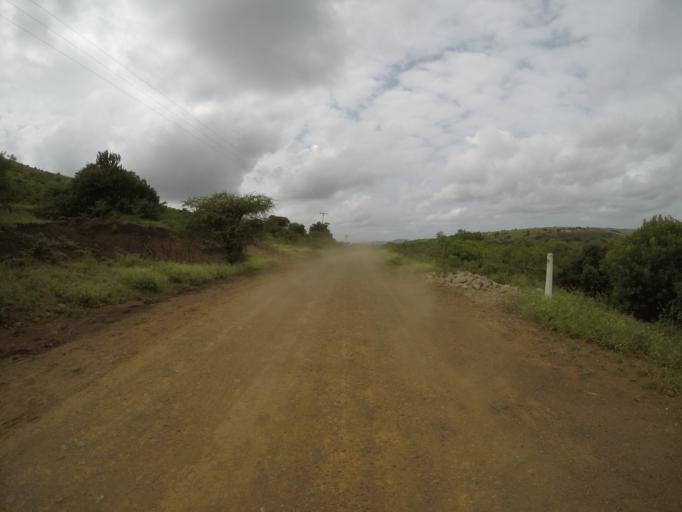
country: ZA
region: KwaZulu-Natal
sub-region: uThungulu District Municipality
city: Empangeni
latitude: -28.6088
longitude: 31.8961
